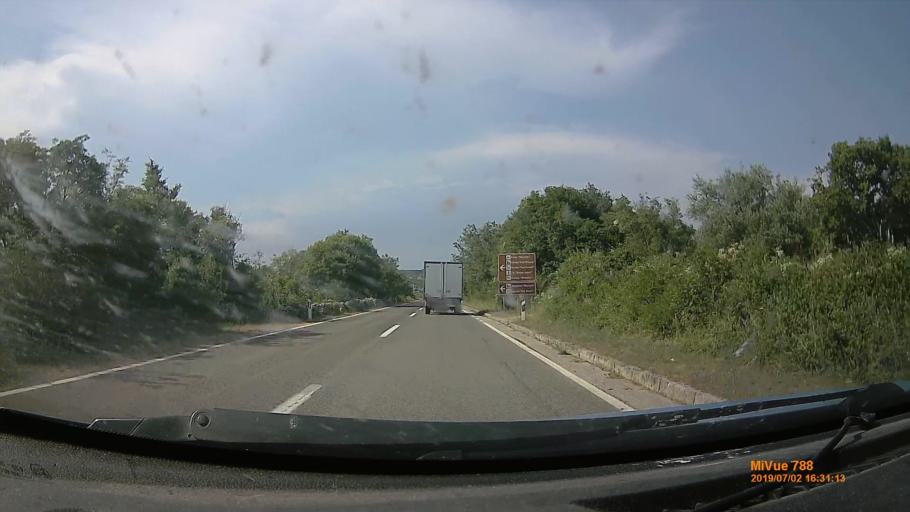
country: HR
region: Primorsko-Goranska
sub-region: Grad Krk
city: Krk
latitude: 45.0514
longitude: 14.4881
